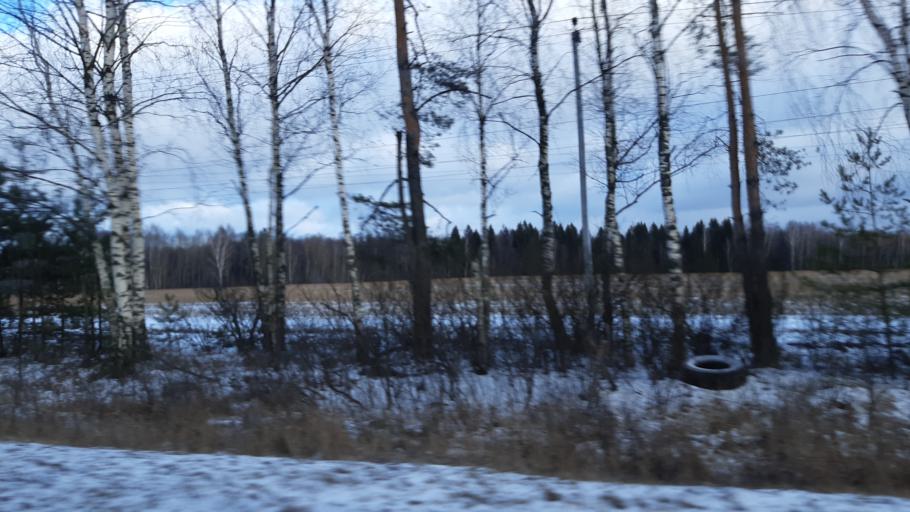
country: RU
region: Moskovskaya
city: Noginsk-9
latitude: 56.0325
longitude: 38.5546
